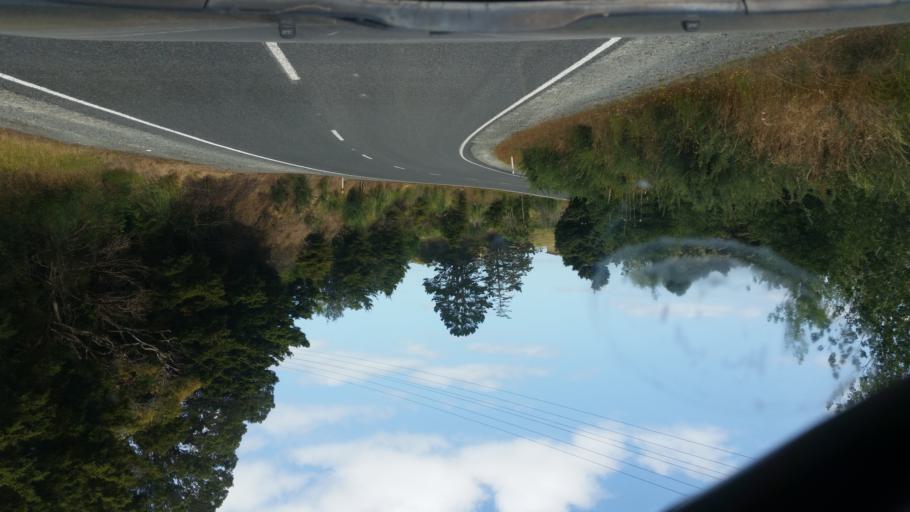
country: NZ
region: Northland
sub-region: Whangarei
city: Ruakaka
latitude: -36.0834
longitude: 174.2396
